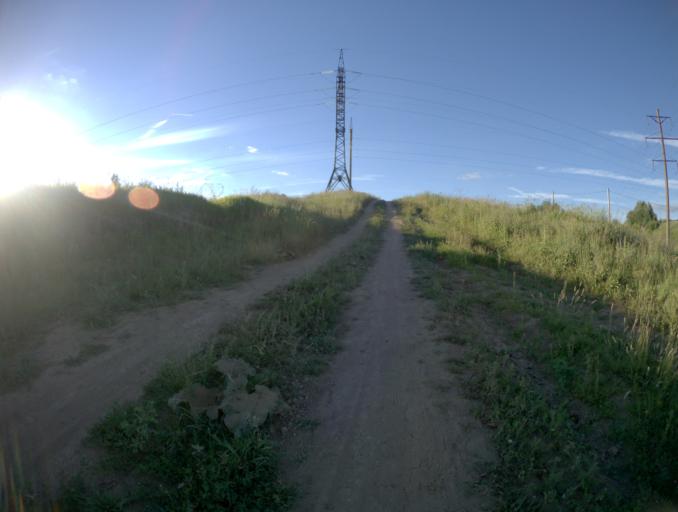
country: RU
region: Vladimir
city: Bogolyubovo
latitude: 56.1854
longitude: 40.5036
